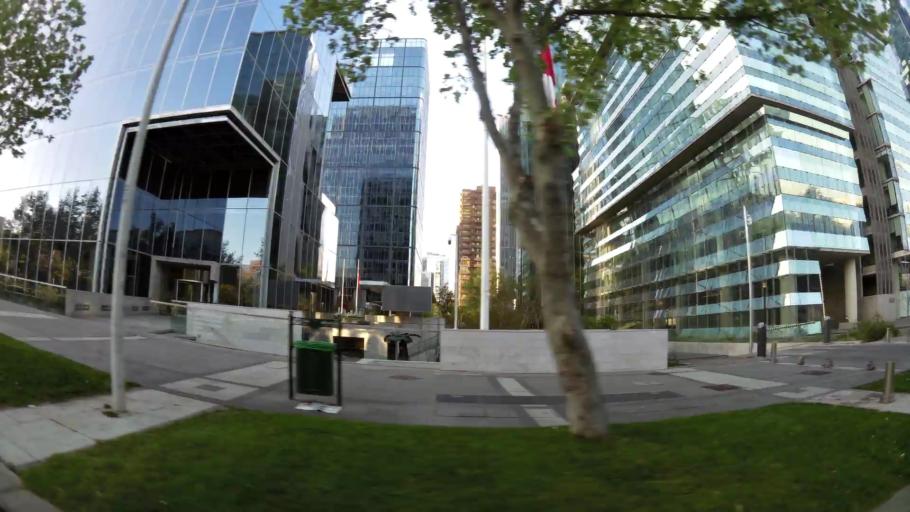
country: CL
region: Santiago Metropolitan
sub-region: Provincia de Santiago
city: Villa Presidente Frei, Nunoa, Santiago, Chile
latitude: -33.4046
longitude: -70.5740
